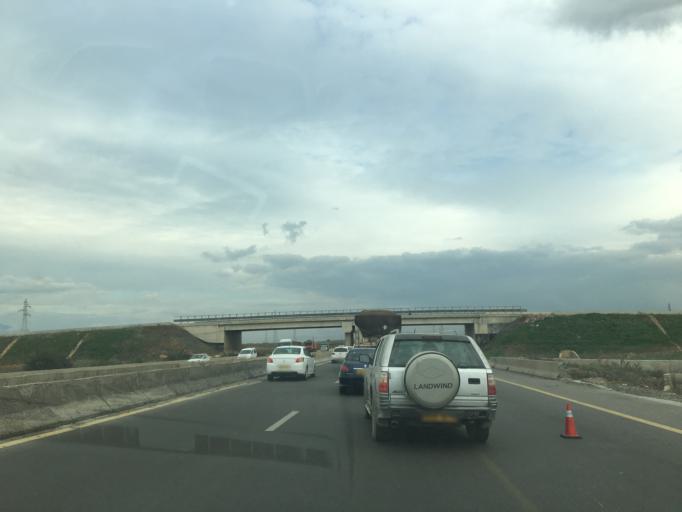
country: DZ
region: Bouira
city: Bouira
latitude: 36.3302
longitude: 3.9433
